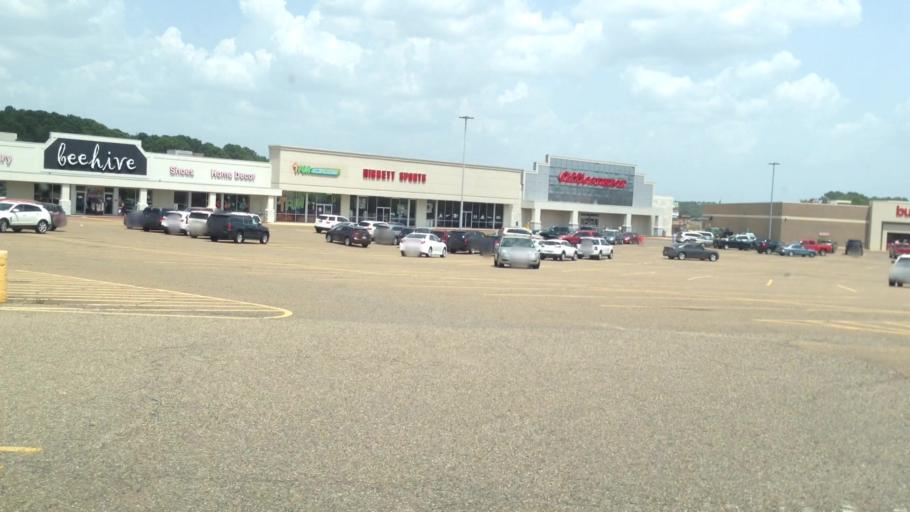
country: US
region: Louisiana
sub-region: Lincoln Parish
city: Ruston
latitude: 32.5420
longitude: -92.6365
